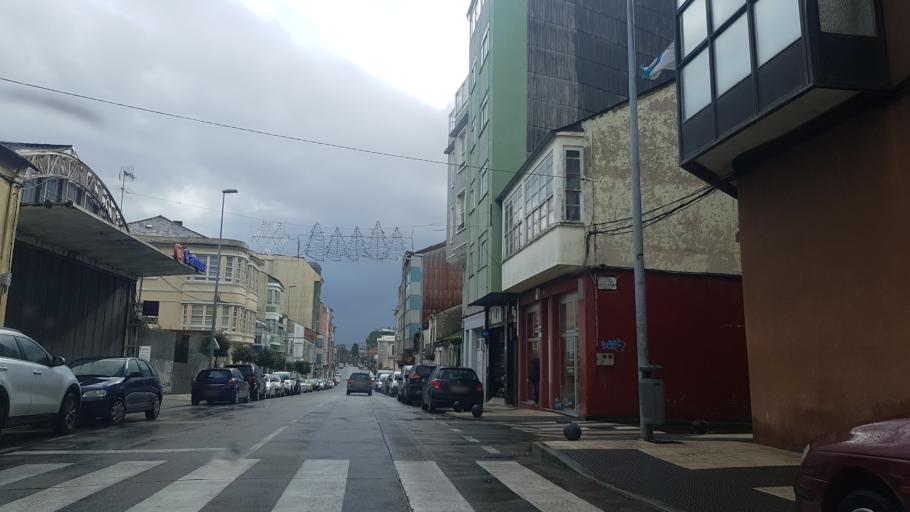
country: ES
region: Galicia
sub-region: Provincia de Lugo
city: Vilalba
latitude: 43.2960
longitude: -7.6814
